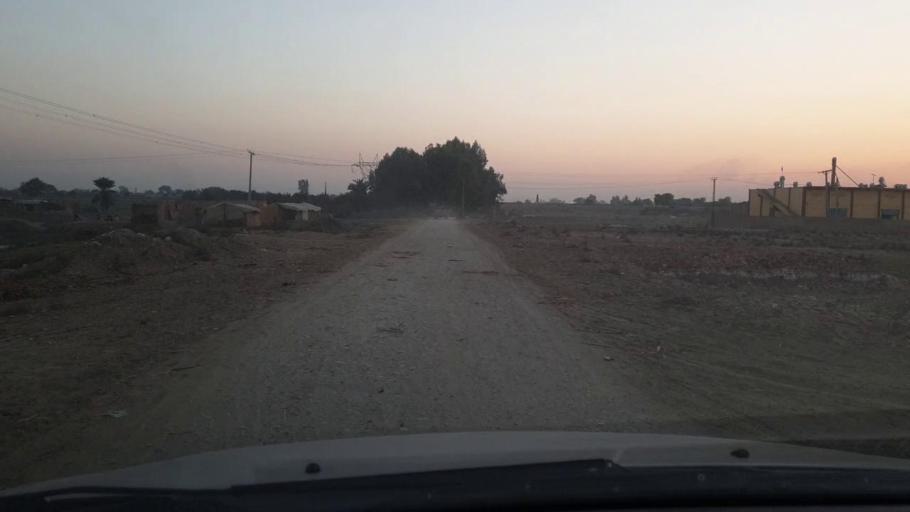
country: PK
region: Sindh
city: Mirpur Mathelo
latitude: 28.0301
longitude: 69.5212
